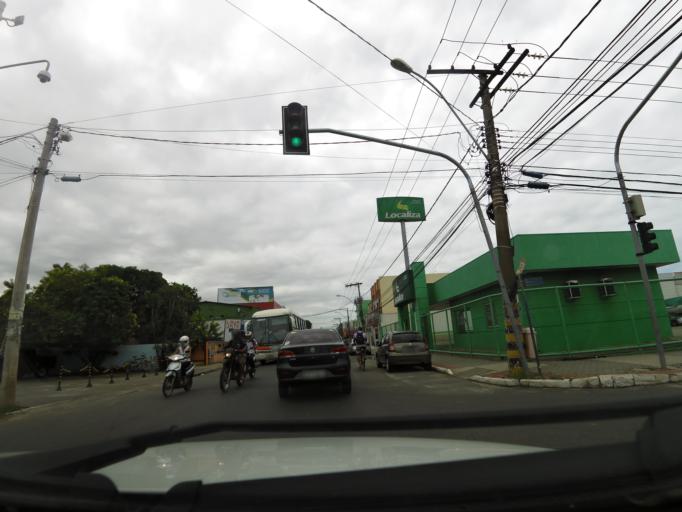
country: BR
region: Espirito Santo
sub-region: Guarapari
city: Guarapari
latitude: -20.6050
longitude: -40.4667
